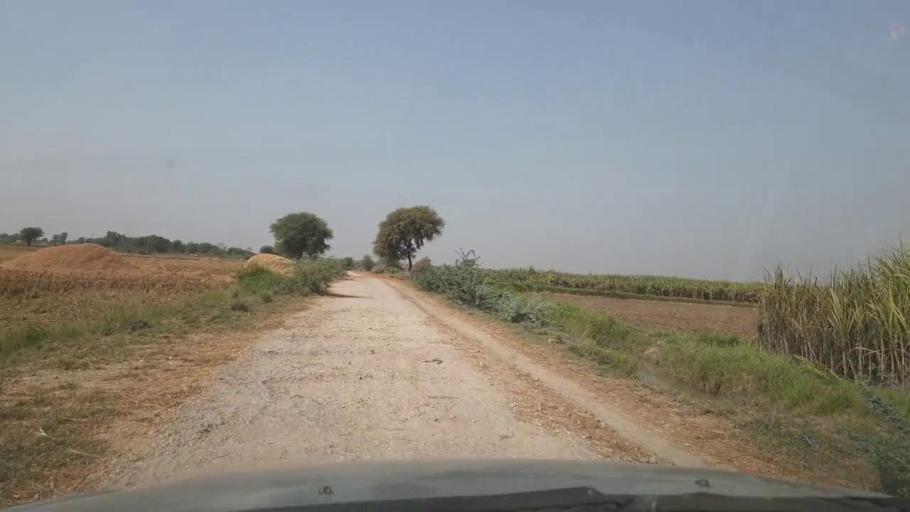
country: PK
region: Sindh
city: Bulri
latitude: 24.8700
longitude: 68.3217
